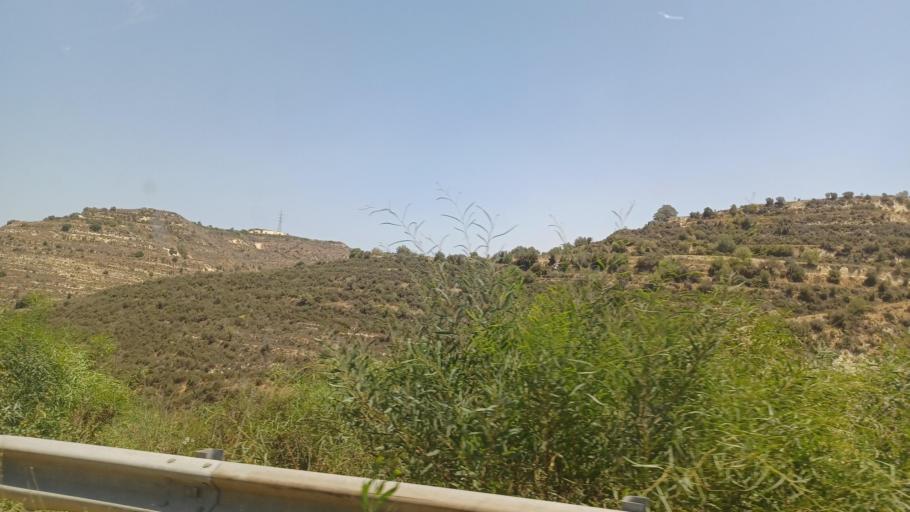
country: CY
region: Pafos
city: Mesogi
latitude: 34.8507
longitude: 32.4799
